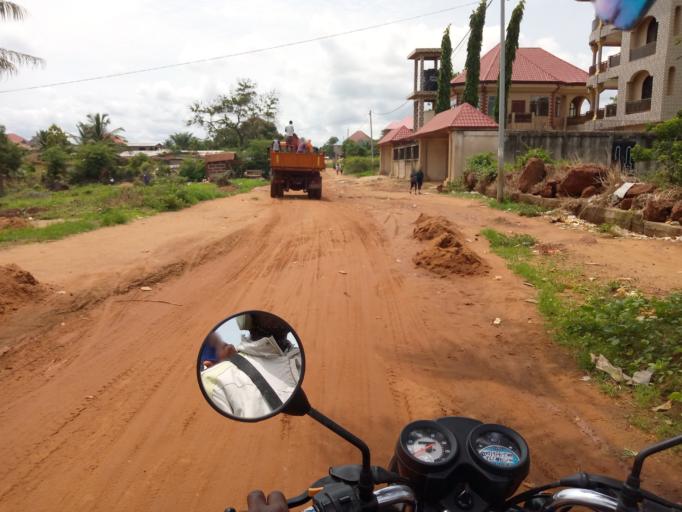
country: SL
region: Western Area
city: Waterloo
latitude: 8.3595
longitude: -13.0759
